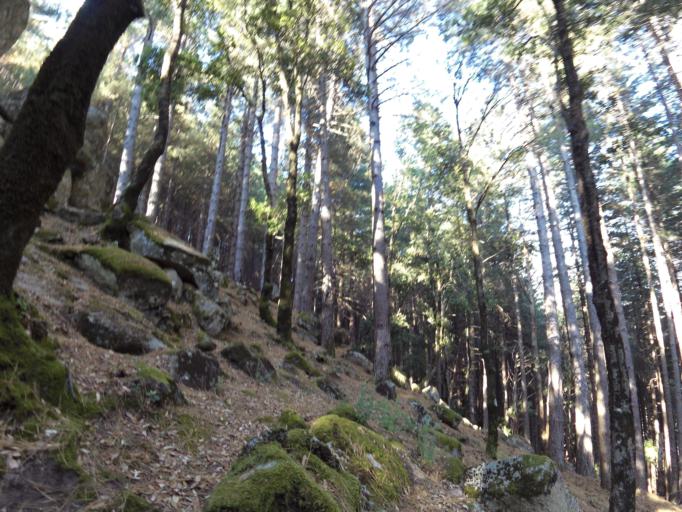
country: IT
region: Calabria
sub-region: Provincia di Vibo-Valentia
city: Nardodipace
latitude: 38.4620
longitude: 16.3490
